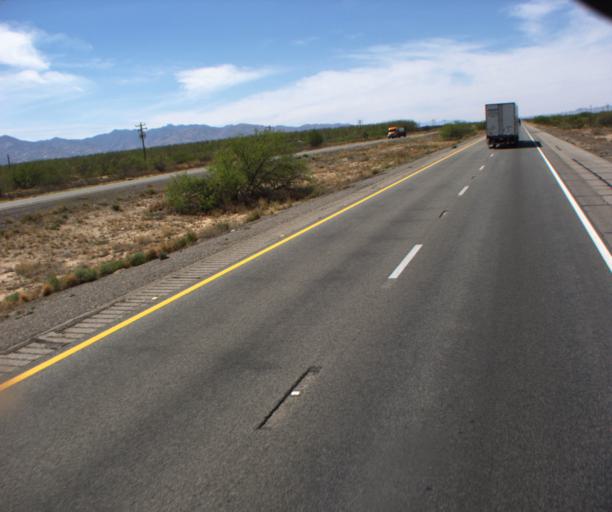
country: US
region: Arizona
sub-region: Cochise County
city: Willcox
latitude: 32.2928
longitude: -109.3336
